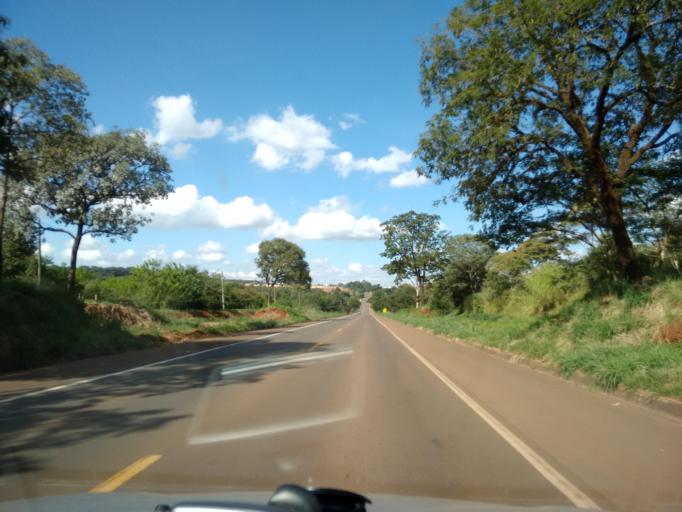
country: BR
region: Sao Paulo
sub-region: Sao Carlos
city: Sao Carlos
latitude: -22.0657
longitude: -47.9184
